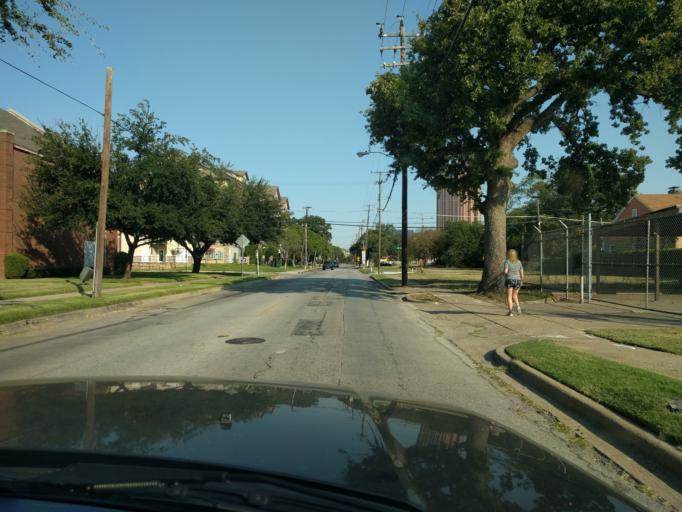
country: US
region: Texas
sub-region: Dallas County
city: Dallas
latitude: 32.7990
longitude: -96.7875
